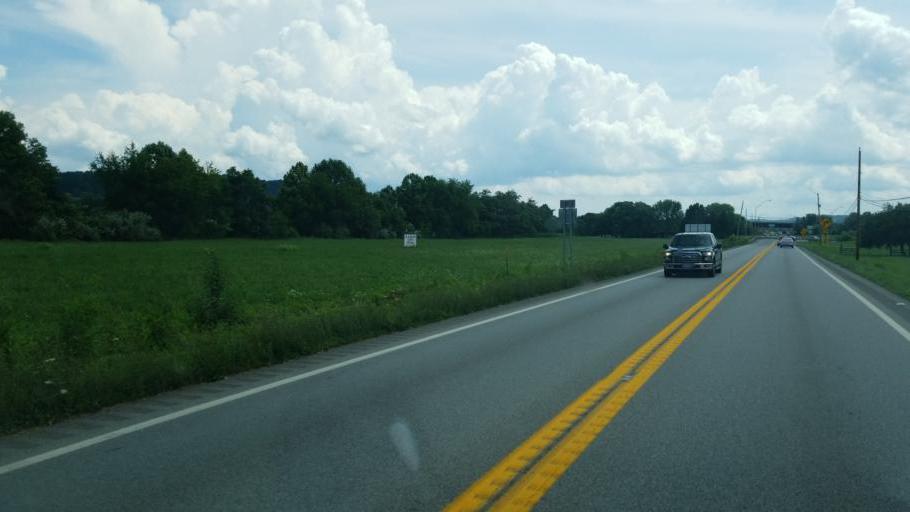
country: US
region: West Virginia
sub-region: Putnam County
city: Buffalo
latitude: 38.5867
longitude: -82.0041
